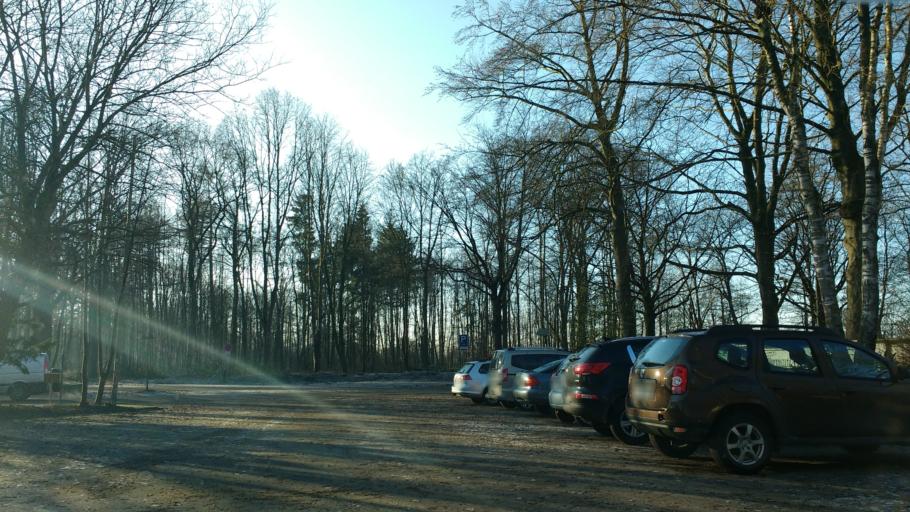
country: DE
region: Schleswig-Holstein
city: Neumunster
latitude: 54.0899
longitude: 9.9462
